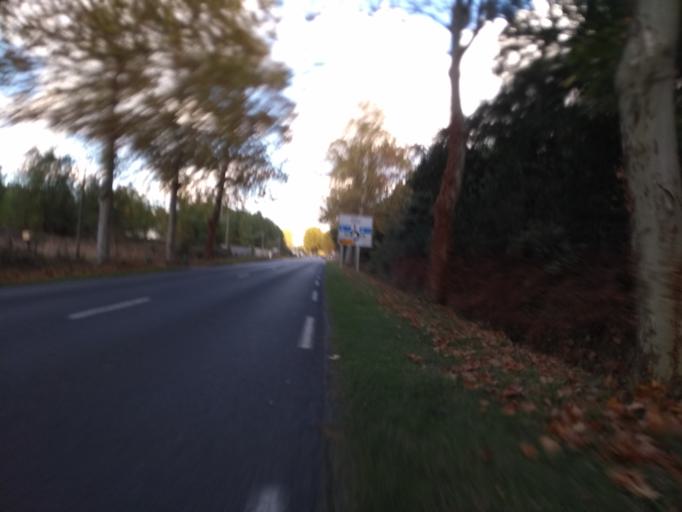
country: FR
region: Aquitaine
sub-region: Departement de la Gironde
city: Saint-Aubin-de-Medoc
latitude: 44.6989
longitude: -0.7077
